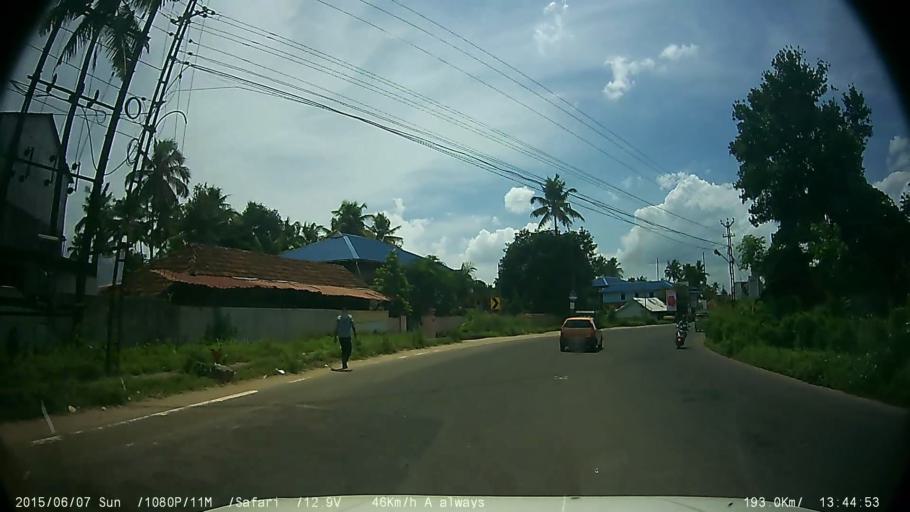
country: IN
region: Kerala
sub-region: Ernakulam
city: Perumpavur
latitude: 10.1276
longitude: 76.4723
